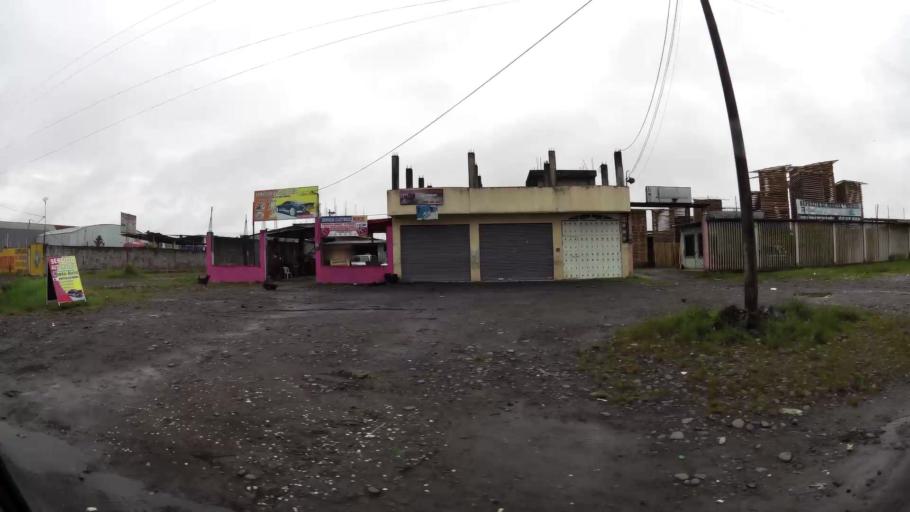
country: EC
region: Santo Domingo de los Tsachilas
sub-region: Canton Santo Domingo de los Colorados
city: Santo Domingo de los Colorados
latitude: -0.2378
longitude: -79.1748
